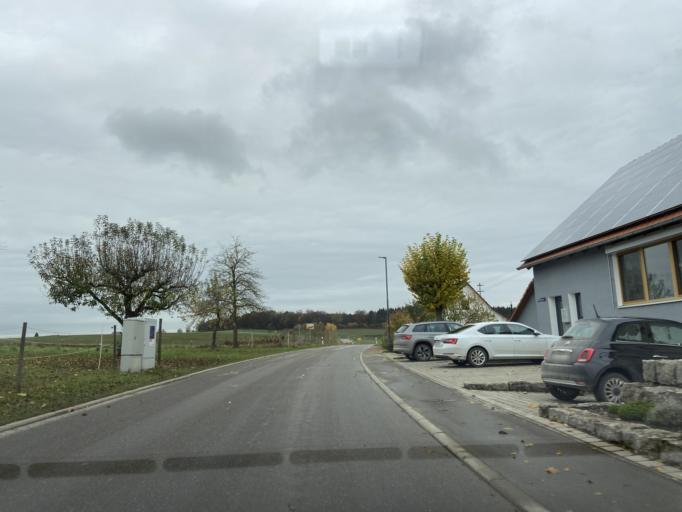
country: DE
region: Baden-Wuerttemberg
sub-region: Tuebingen Region
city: Wald
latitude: 47.9662
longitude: 9.2039
